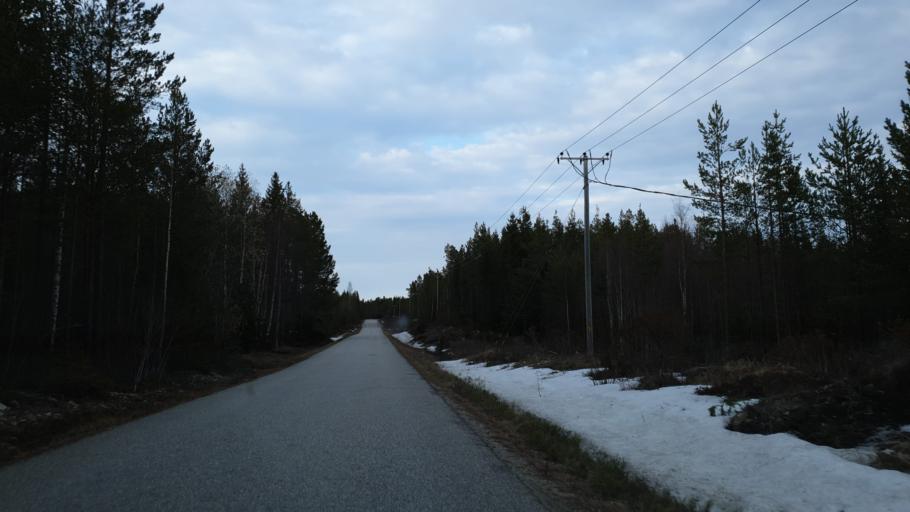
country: SE
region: Vaesternorrland
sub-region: Sundsvalls Kommun
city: Njurundabommen
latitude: 61.9933
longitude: 17.3822
